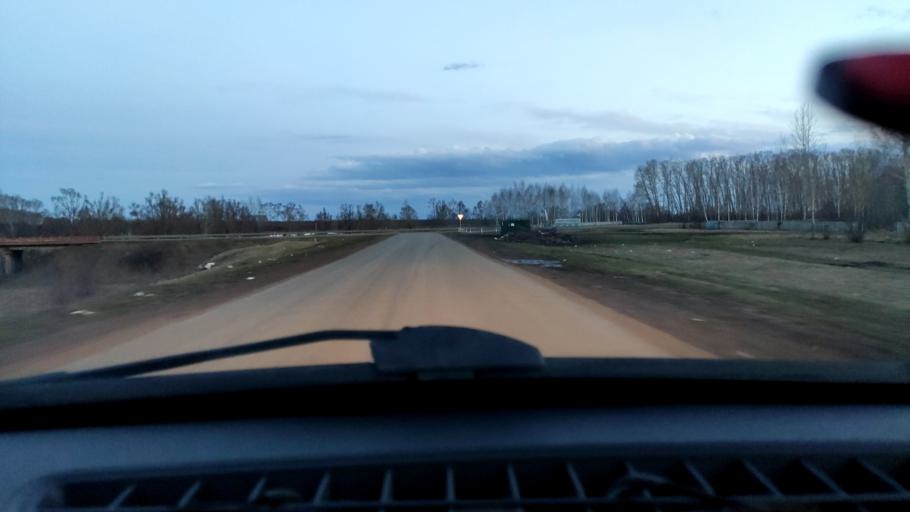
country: RU
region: Bashkortostan
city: Ulukulevo
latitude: 54.4186
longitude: 56.3431
